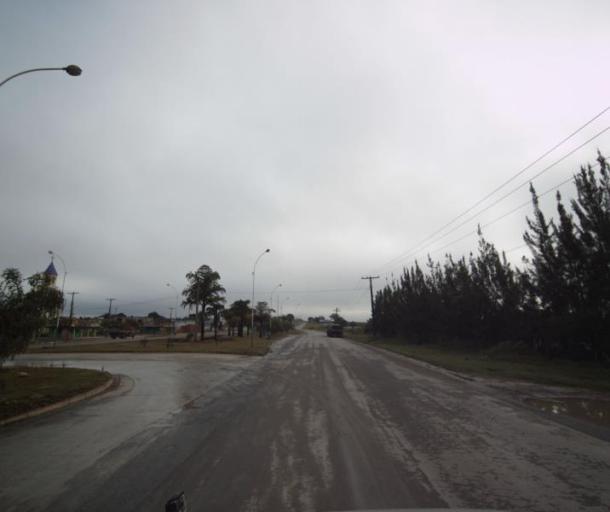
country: BR
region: Goias
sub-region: Pirenopolis
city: Pirenopolis
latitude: -15.7858
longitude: -48.7699
